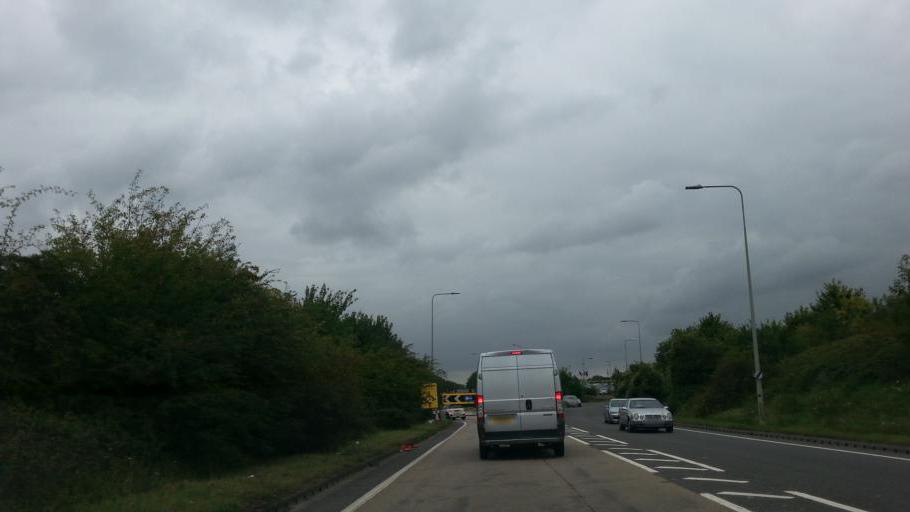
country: GB
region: England
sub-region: Essex
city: Chelmsford
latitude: 51.7766
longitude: 0.4880
